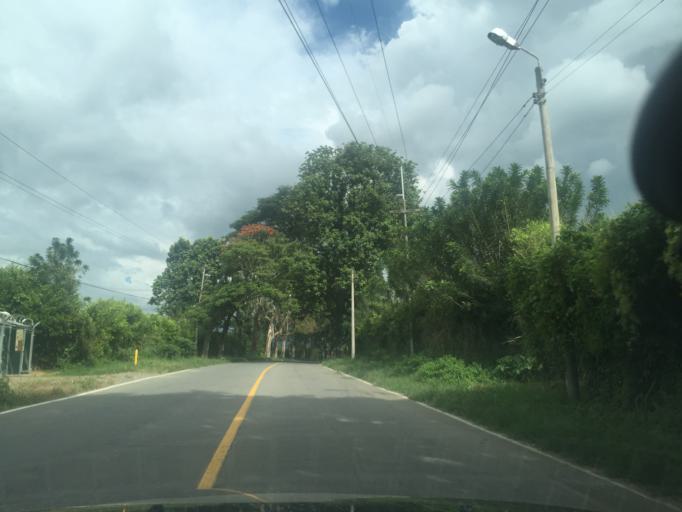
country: CO
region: Valle del Cauca
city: Caicedonia
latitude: 4.3418
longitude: -75.8363
